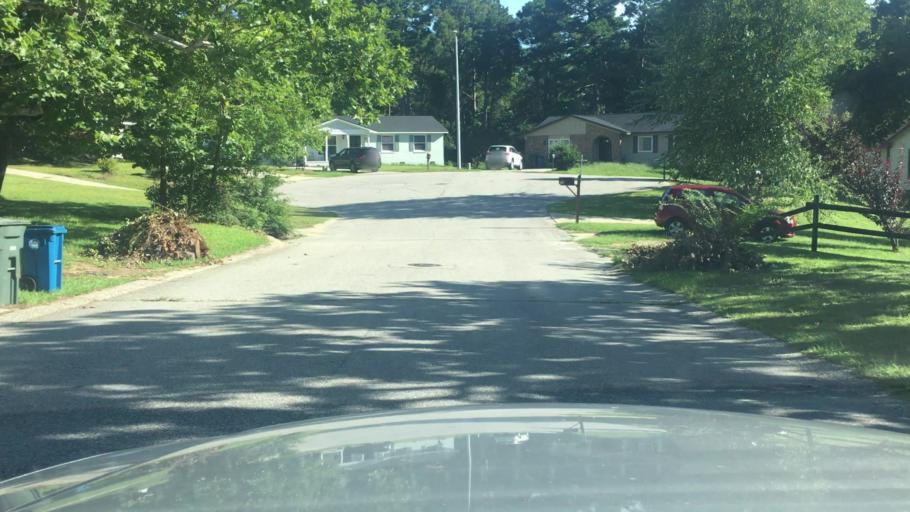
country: US
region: North Carolina
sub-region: Cumberland County
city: Fayetteville
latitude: 35.1379
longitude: -78.8909
